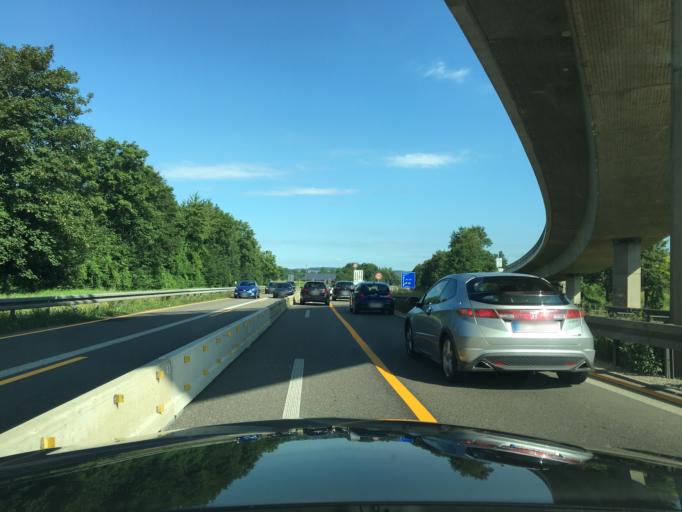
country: DE
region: Bavaria
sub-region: Swabia
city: Neu-Ulm
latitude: 48.3713
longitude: 9.9953
